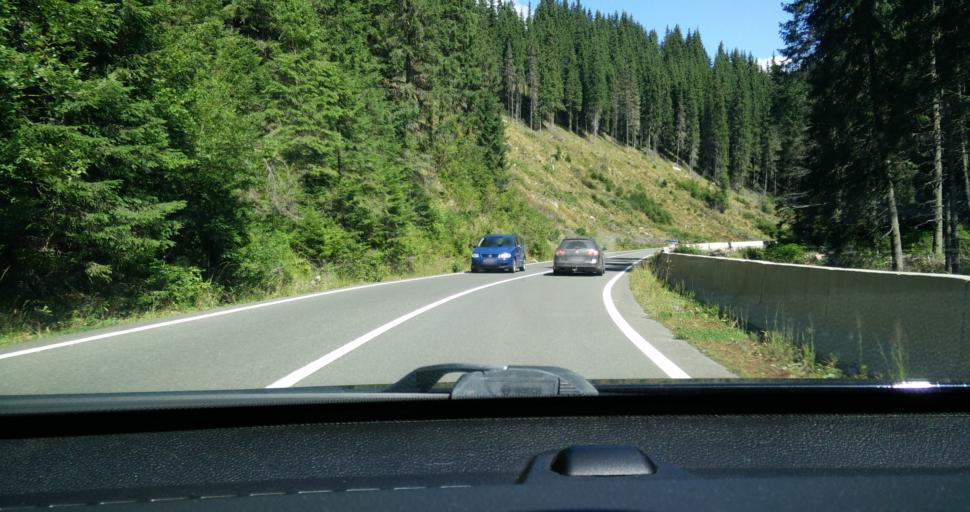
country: RO
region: Hunedoara
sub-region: Oras Petrila
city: Petrila
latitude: 45.5162
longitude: 23.6504
